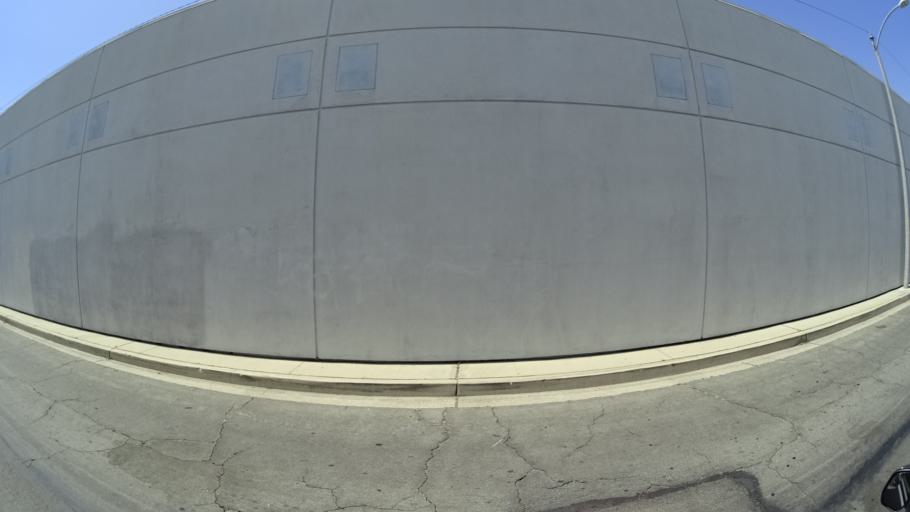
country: US
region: California
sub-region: Los Angeles County
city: Burbank
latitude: 34.2023
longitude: -118.3428
